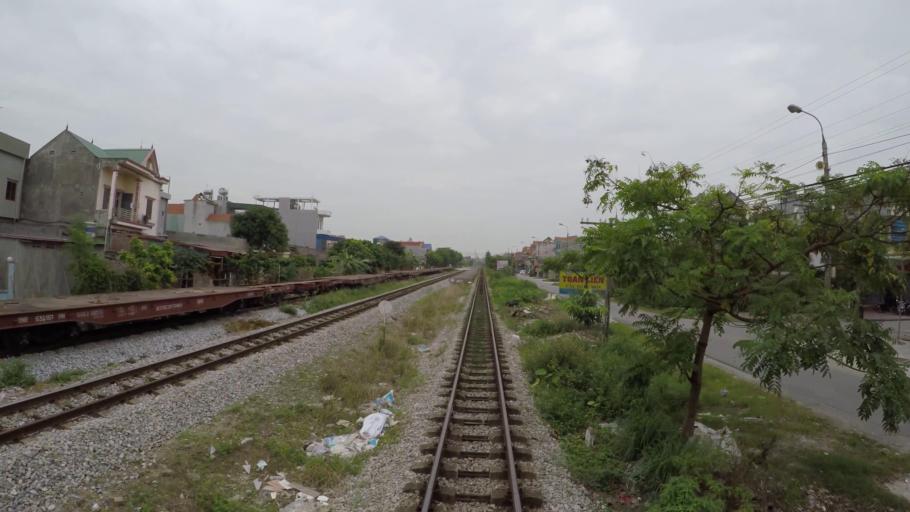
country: VN
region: Hai Duong
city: Phu Thai
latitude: 20.9732
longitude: 106.4811
